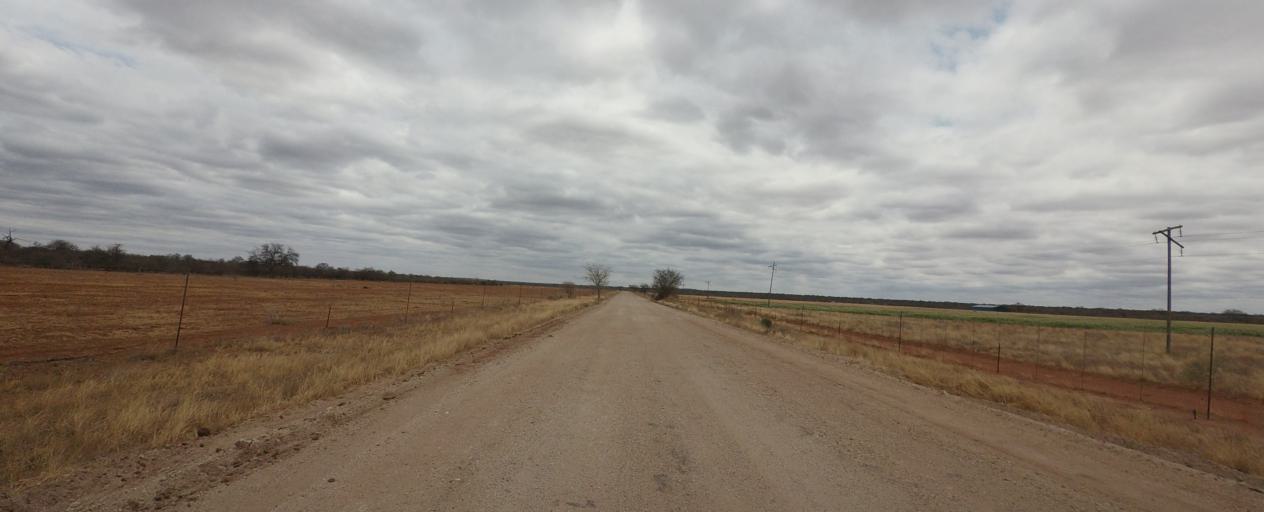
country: BW
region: Central
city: Mathathane
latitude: -22.7097
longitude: 28.5755
